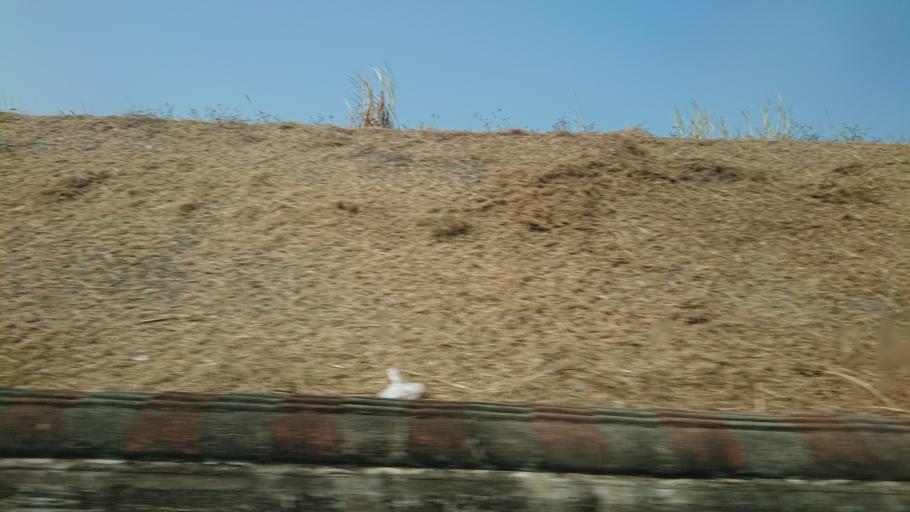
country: TW
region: Taiwan
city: Lugu
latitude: 23.7481
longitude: 120.6587
